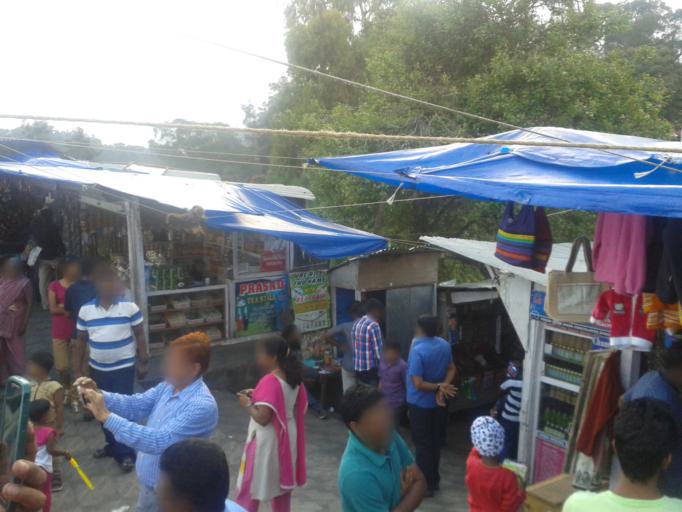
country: IN
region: Tamil Nadu
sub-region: Dindigul
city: Kodaikanal
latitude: 10.2100
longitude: 77.4759
